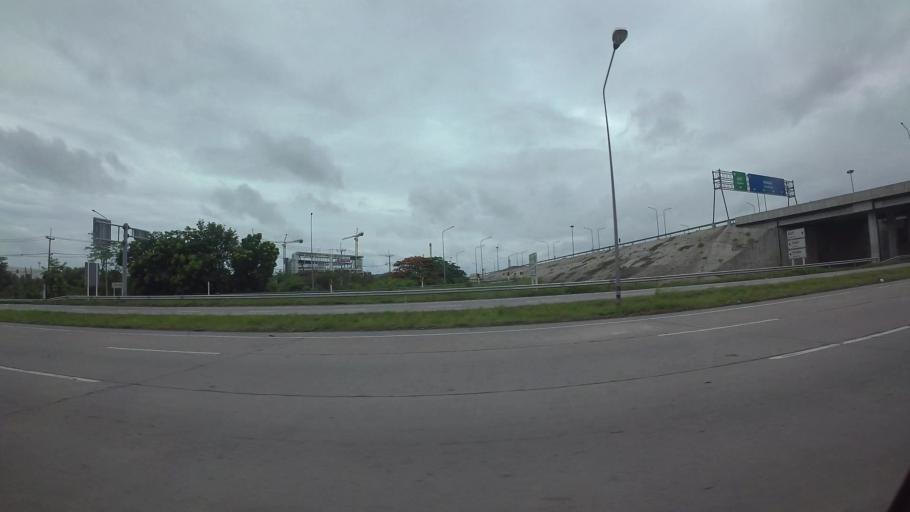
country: TH
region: Chon Buri
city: Bang Lamung
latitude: 13.1034
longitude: 100.9162
